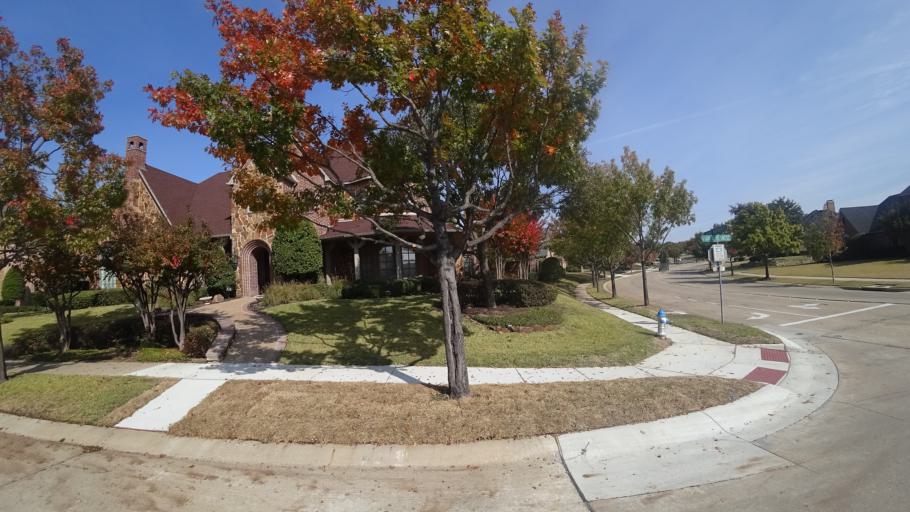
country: US
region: Texas
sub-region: Denton County
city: The Colony
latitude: 33.0365
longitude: -96.8976
